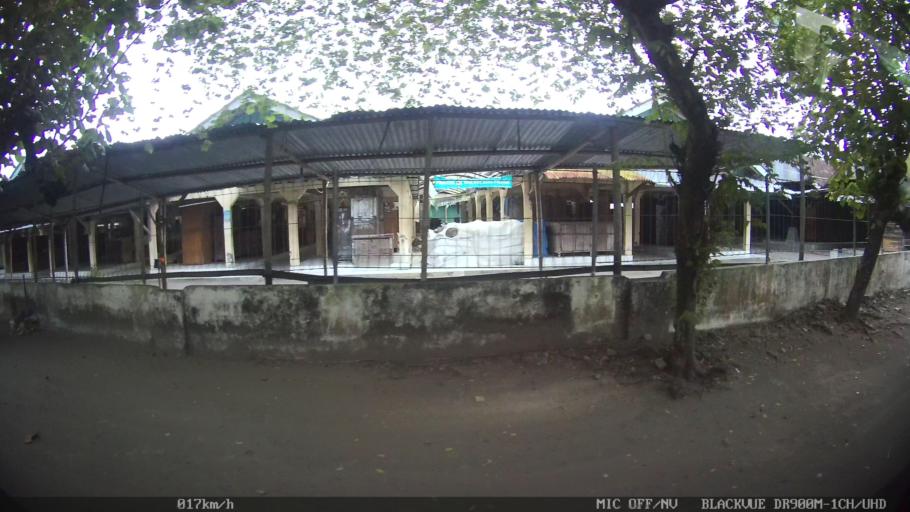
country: ID
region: Daerah Istimewa Yogyakarta
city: Sewon
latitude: -7.8657
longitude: 110.4074
